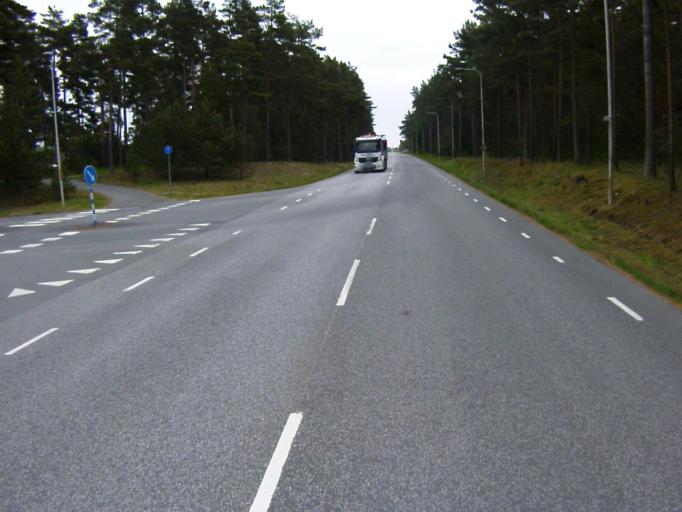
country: SE
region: Skane
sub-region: Kristianstads Kommun
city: Ahus
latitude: 55.9352
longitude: 14.2751
